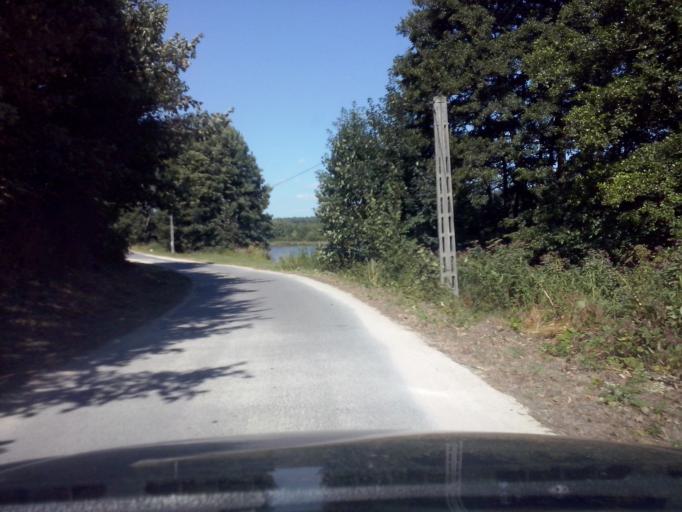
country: PL
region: Swietokrzyskie
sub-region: Powiat buski
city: Gnojno
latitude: 50.6236
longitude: 20.8799
